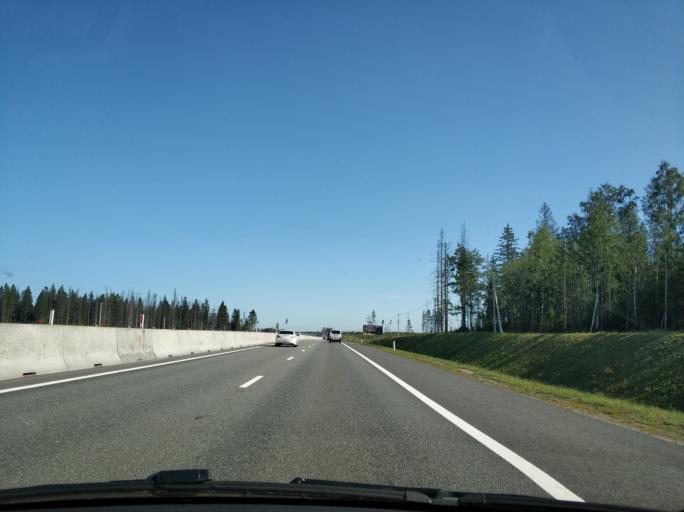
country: RU
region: Leningrad
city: Sosnovo
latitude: 60.4910
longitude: 30.1959
